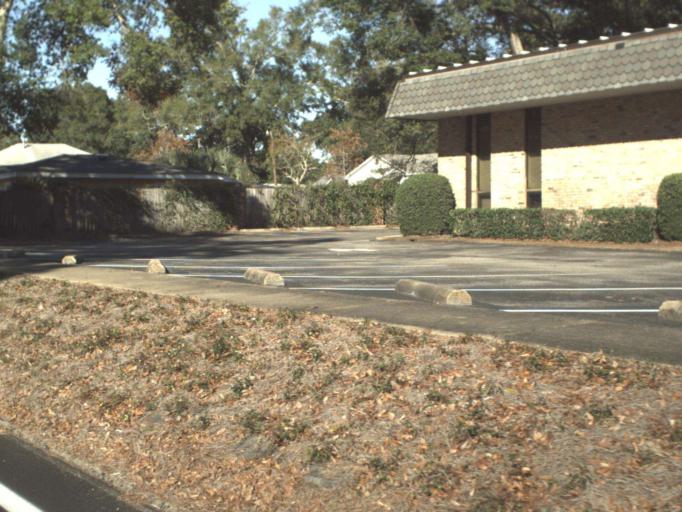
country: US
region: Florida
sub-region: Escambia County
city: Pensacola
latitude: 30.4337
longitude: -87.2094
